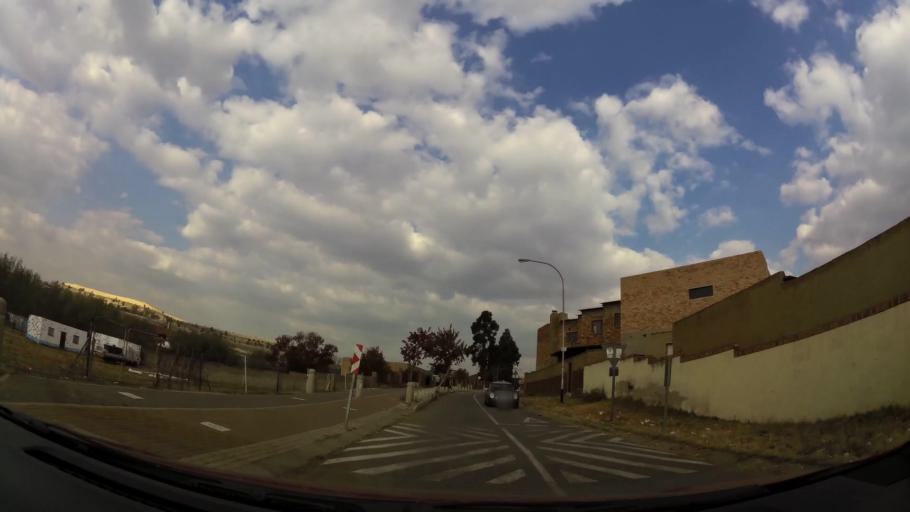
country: ZA
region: Gauteng
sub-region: City of Johannesburg Metropolitan Municipality
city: Roodepoort
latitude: -26.2241
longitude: 27.9347
